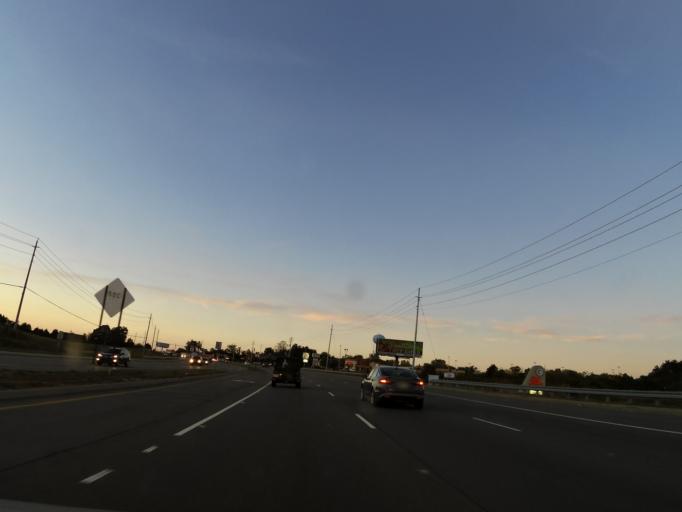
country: US
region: Tennessee
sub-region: Sevier County
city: Sevierville
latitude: 35.9601
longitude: -83.5939
